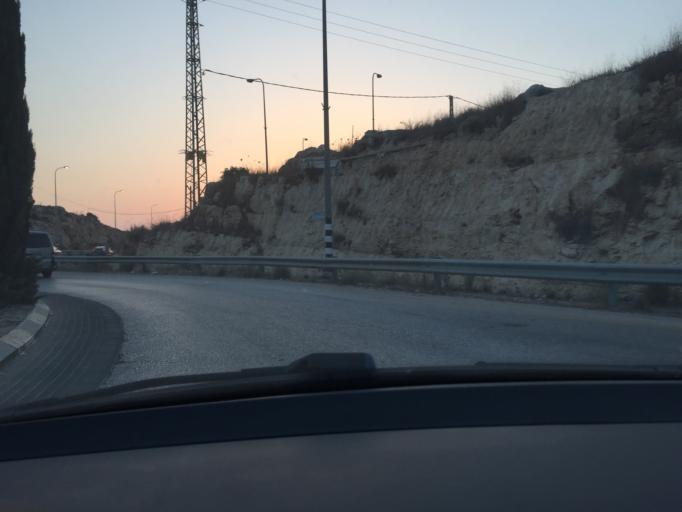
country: PS
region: West Bank
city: Kafr ad Dik
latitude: 32.0670
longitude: 35.0638
